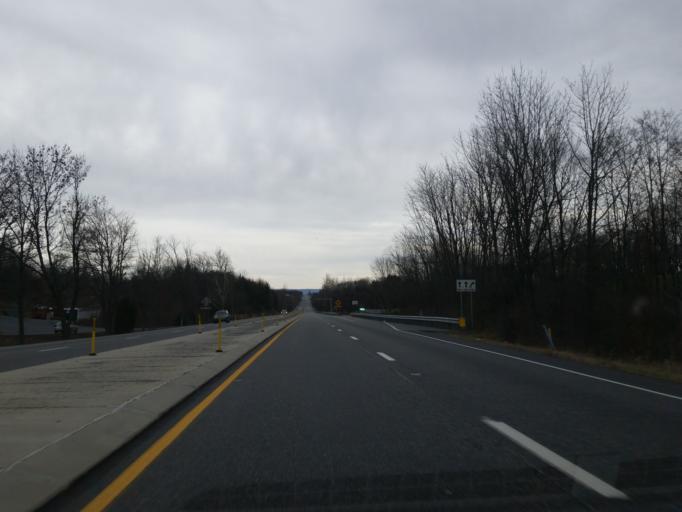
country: US
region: Pennsylvania
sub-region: Dauphin County
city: Skyline View
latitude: 40.3598
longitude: -76.6713
